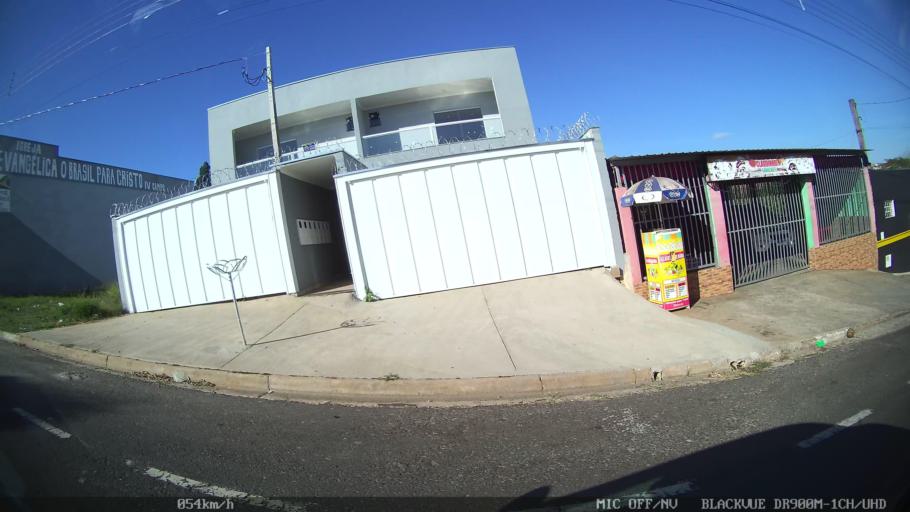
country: BR
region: Sao Paulo
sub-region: Franca
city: Franca
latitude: -20.4879
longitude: -47.4287
